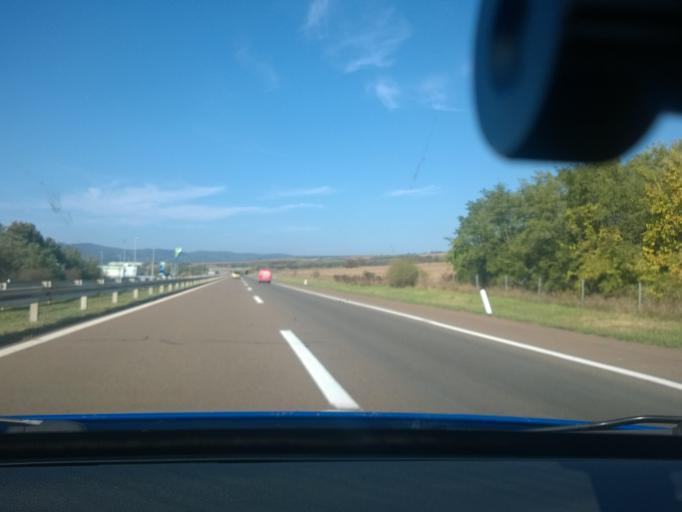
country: RS
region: Central Serbia
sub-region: Nisavski Okrug
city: Razanj
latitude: 43.6160
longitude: 21.5945
